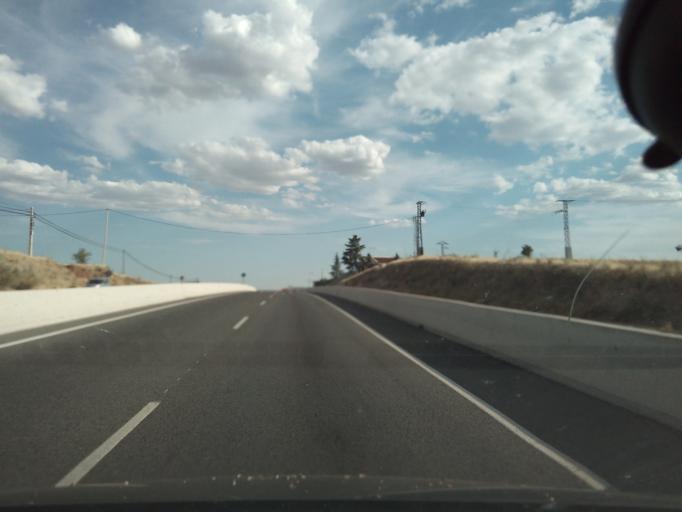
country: ES
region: Madrid
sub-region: Provincia de Madrid
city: Ajalvir
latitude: 40.5181
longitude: -3.4811
